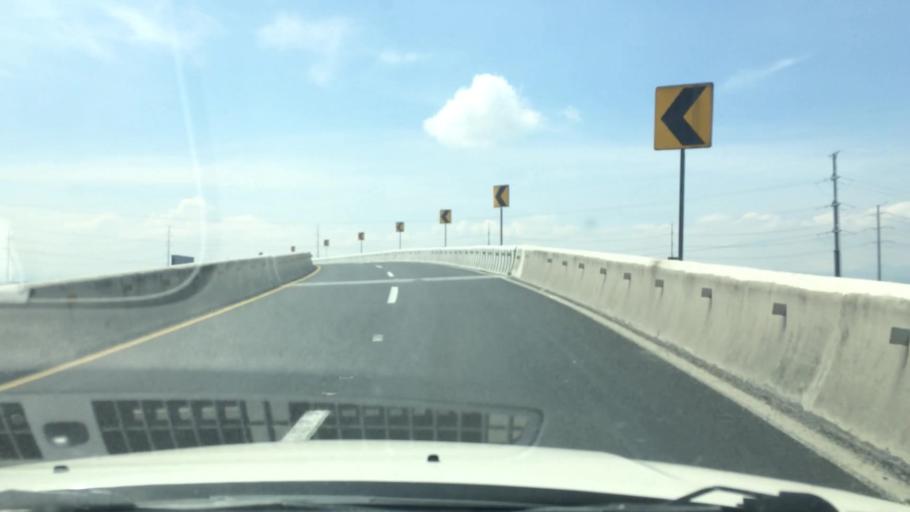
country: MX
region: Morelos
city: Lerma de Villada
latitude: 19.2851
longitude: -99.5218
